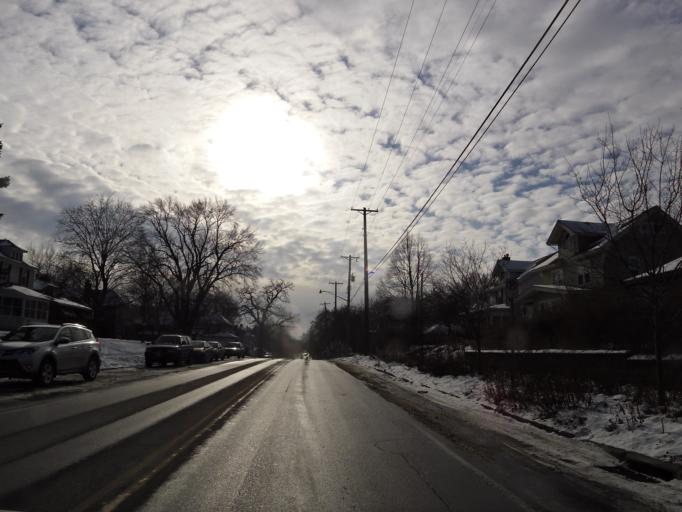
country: US
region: Minnesota
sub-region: Ramsey County
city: Falcon Heights
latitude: 44.9520
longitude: -93.1874
